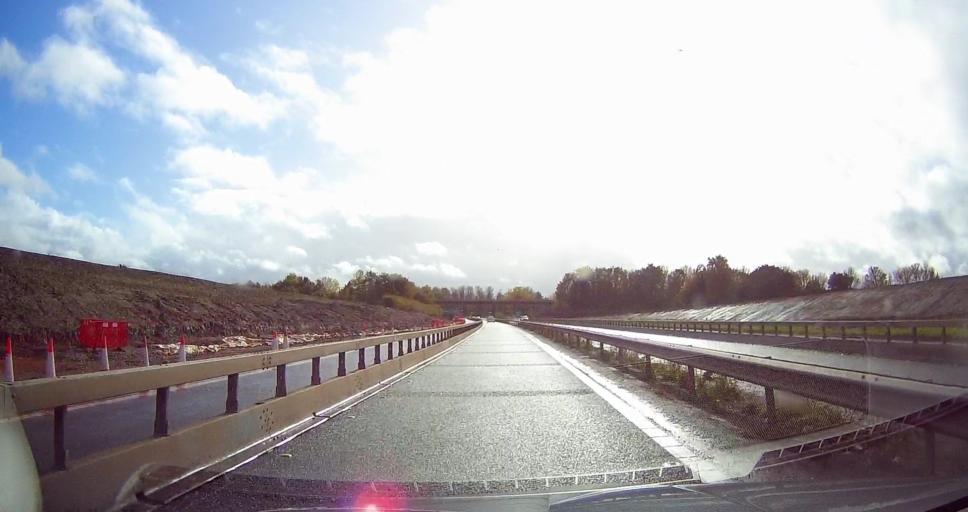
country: GB
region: England
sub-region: Warwickshire
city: Curdworth
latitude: 52.5349
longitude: -1.7776
